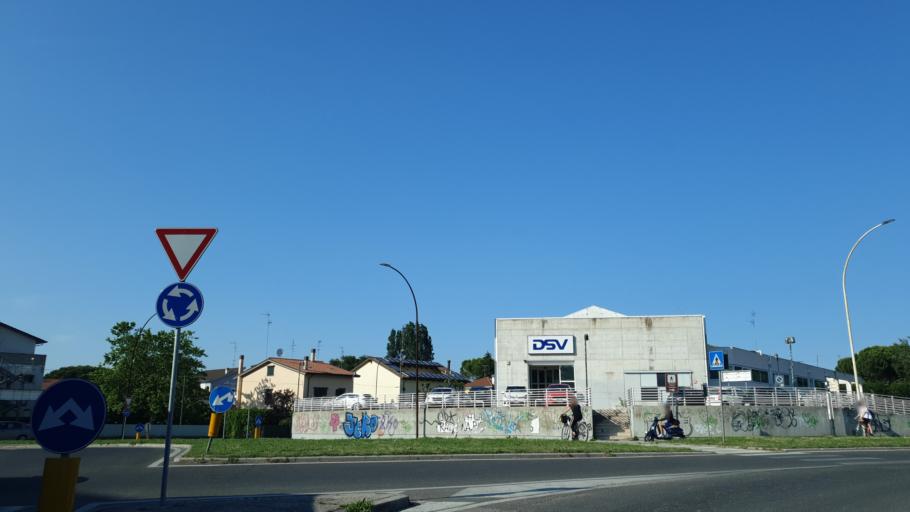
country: IT
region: Emilia-Romagna
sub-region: Provincia di Ravenna
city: Ravenna
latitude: 44.4236
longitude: 12.2040
